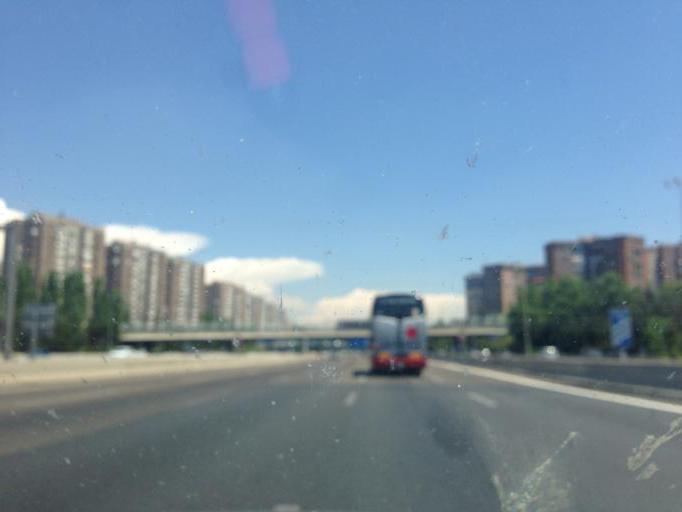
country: ES
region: Madrid
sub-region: Provincia de Madrid
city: Puente de Vallecas
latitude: 40.4071
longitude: -3.6647
